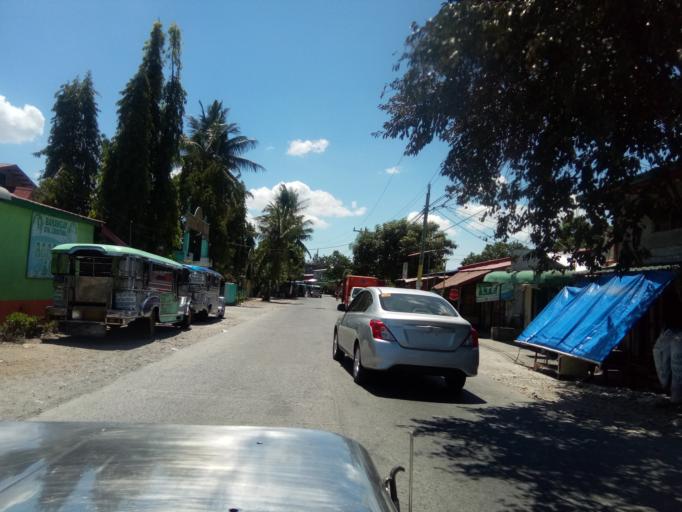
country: PH
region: Calabarzon
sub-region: Province of Cavite
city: Dasmarinas
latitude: 14.3242
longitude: 120.9695
